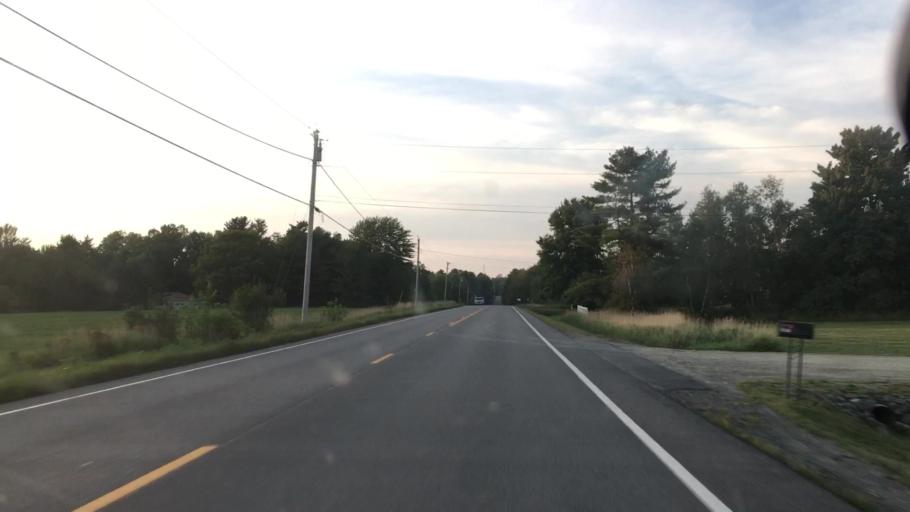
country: US
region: Maine
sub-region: Penobscot County
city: Hermon
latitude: 44.7469
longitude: -68.9676
